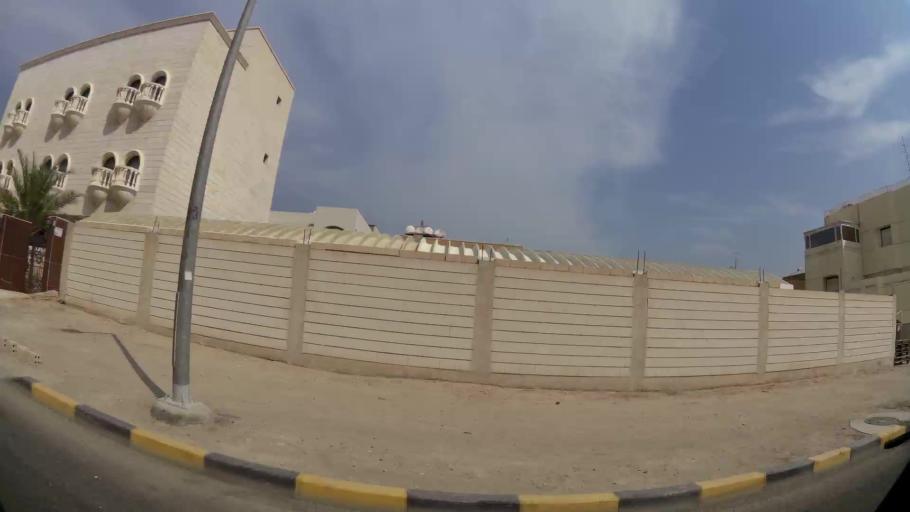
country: KW
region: Al Asimah
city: Ad Dasmah
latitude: 29.3528
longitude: 47.9899
